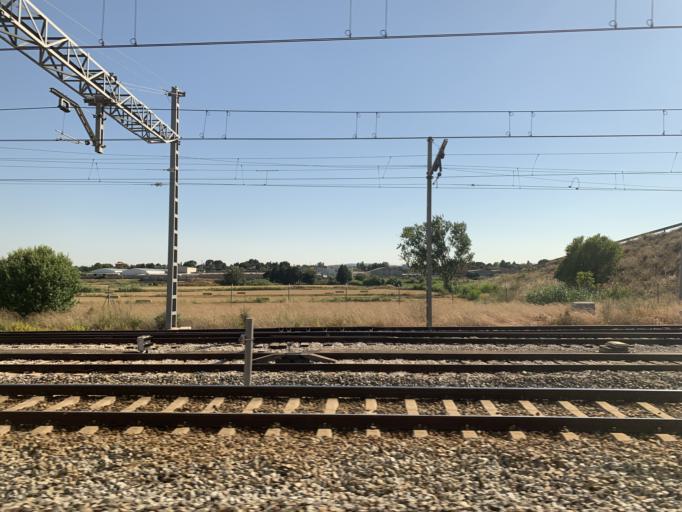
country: ES
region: Aragon
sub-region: Provincia de Zaragoza
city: Oliver-Valdefierro, Oliver, Valdefierro
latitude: 41.6752
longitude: -0.9397
